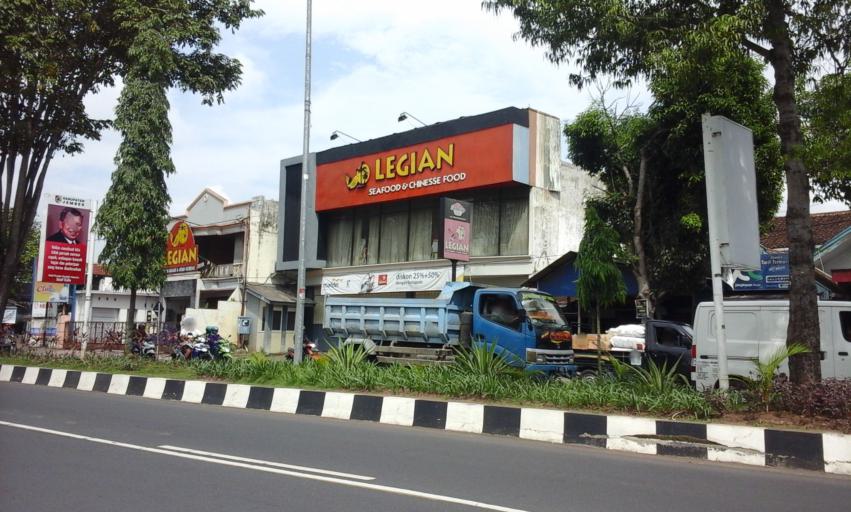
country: ID
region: East Java
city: Kaliwates
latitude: -8.1818
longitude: 113.6735
